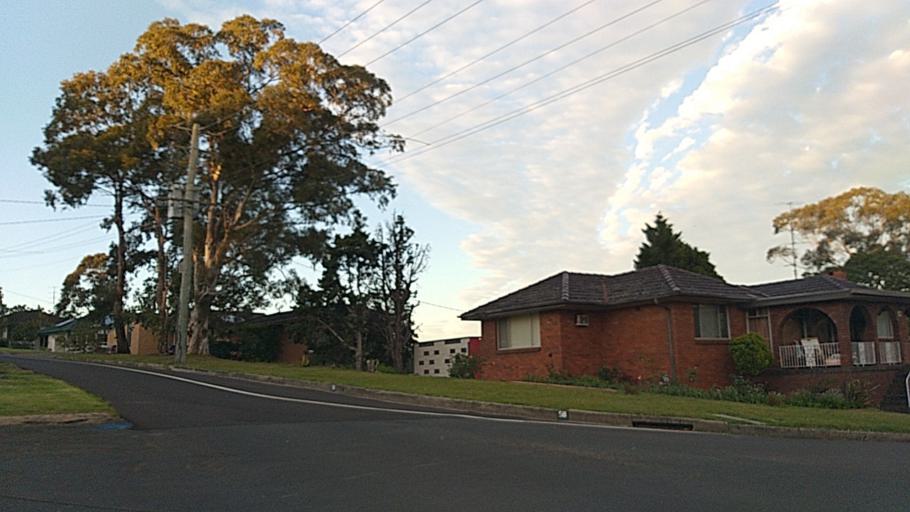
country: AU
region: New South Wales
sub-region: Wollongong
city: Dapto
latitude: -34.5042
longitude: 150.7937
